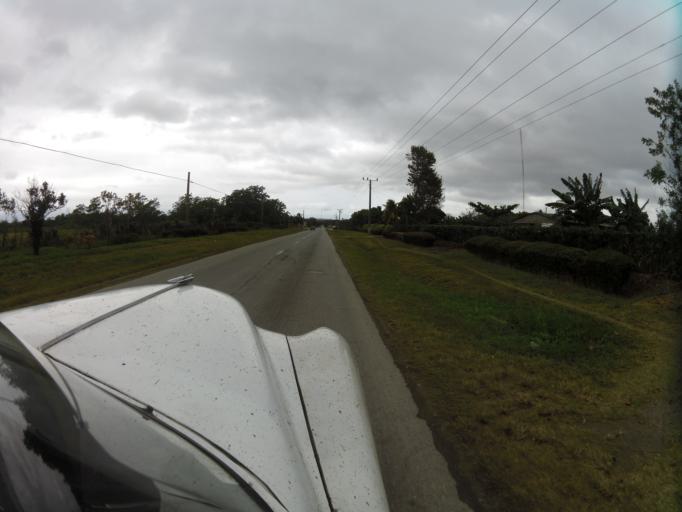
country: CU
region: Las Tunas
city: Las Tunas
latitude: 20.9291
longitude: -76.9075
